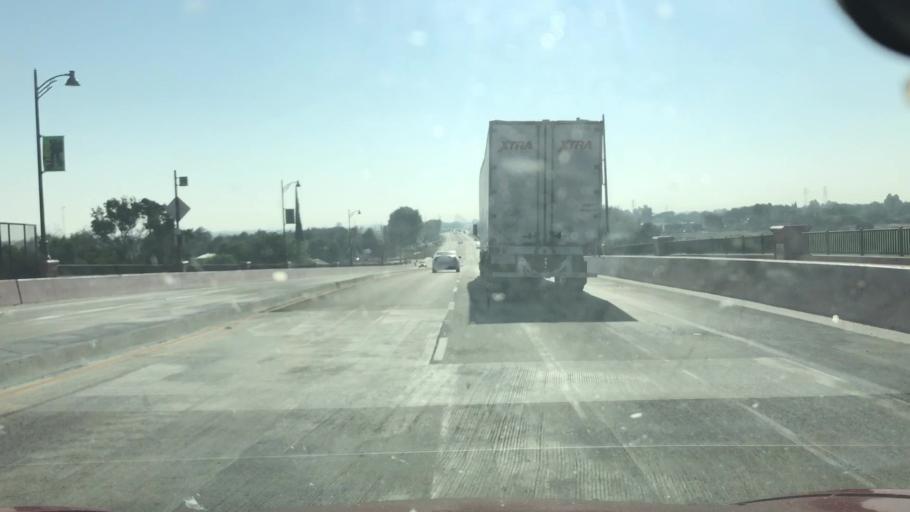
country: US
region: California
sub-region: San Joaquin County
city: Tracy
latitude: 37.7400
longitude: -121.4094
